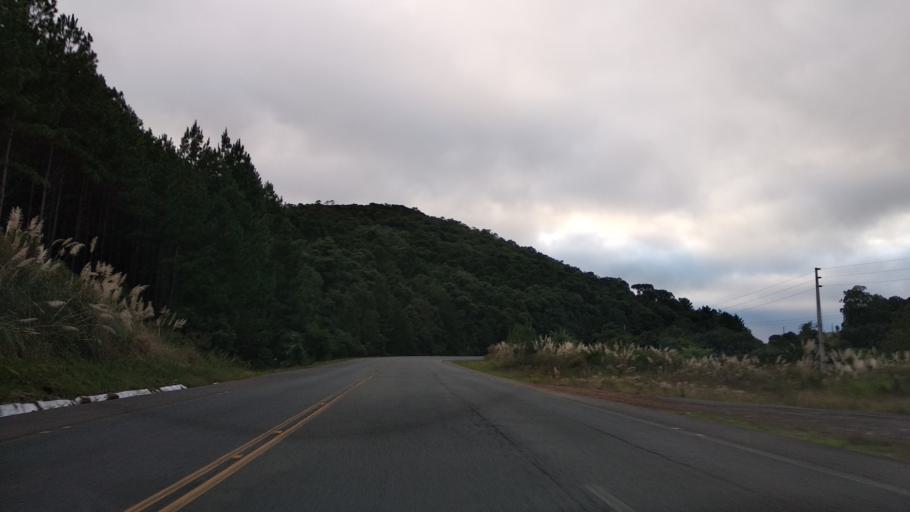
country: BR
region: Santa Catarina
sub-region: Campos Novos
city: Campos Novos
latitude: -27.4931
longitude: -50.9711
